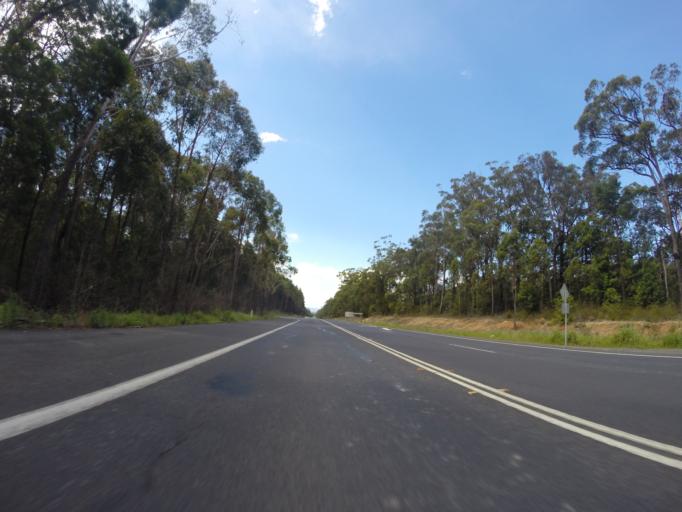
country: AU
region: New South Wales
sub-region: Shoalhaven Shire
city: Falls Creek
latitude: -35.0252
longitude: 150.5785
